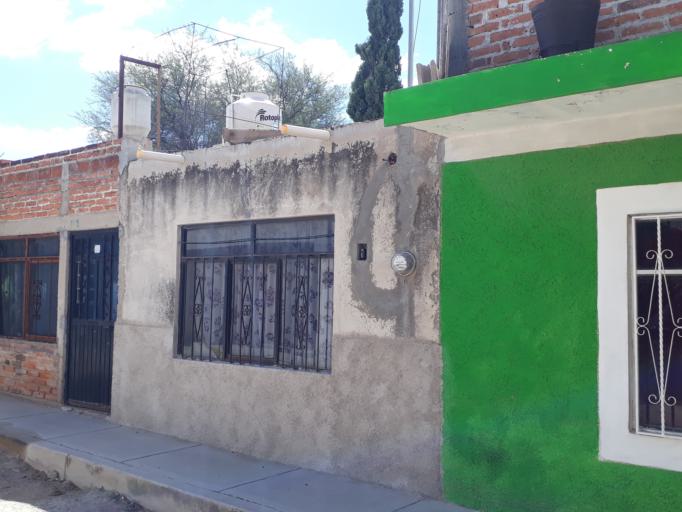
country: MX
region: Aguascalientes
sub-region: Aguascalientes
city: San Sebastian [Fraccionamiento]
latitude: 21.8018
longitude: -102.2735
